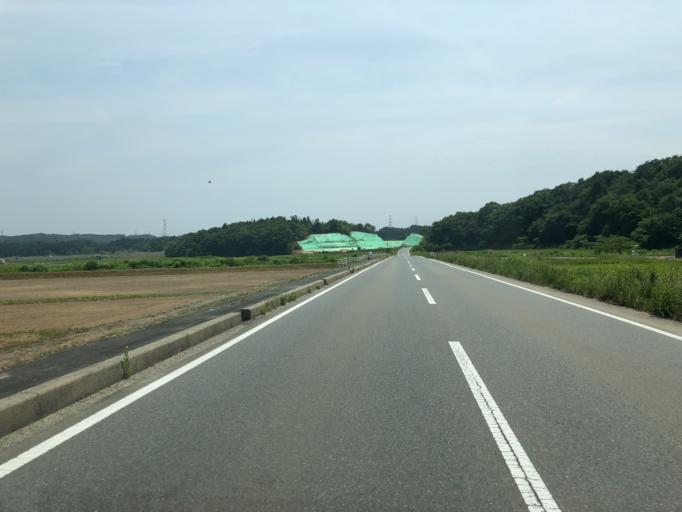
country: JP
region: Fukushima
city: Namie
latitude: 37.5481
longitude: 140.9351
